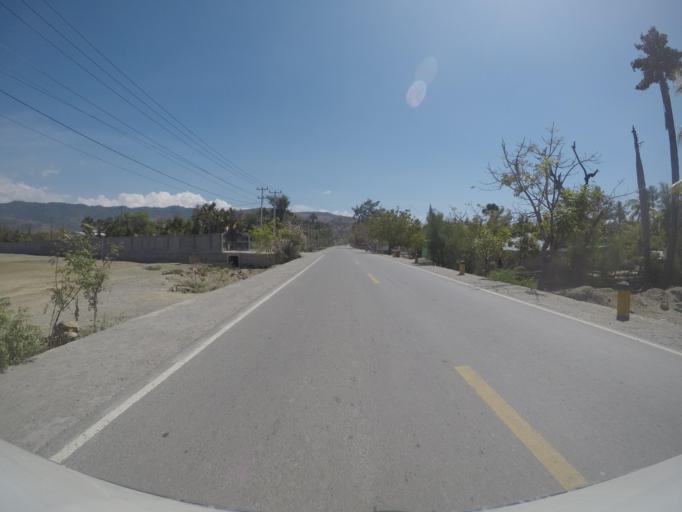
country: TL
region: Dili
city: Dili
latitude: -8.5716
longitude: 125.4634
